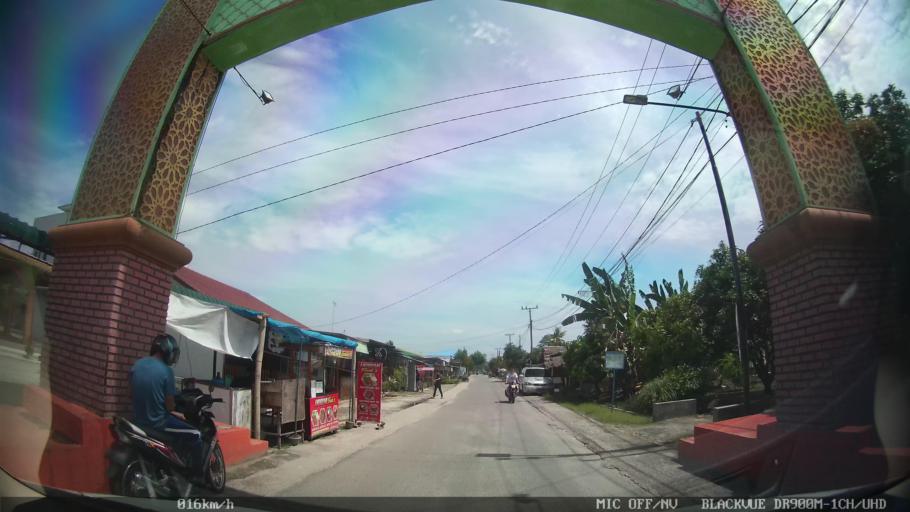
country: ID
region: North Sumatra
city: Percut
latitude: 3.6015
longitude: 98.8605
